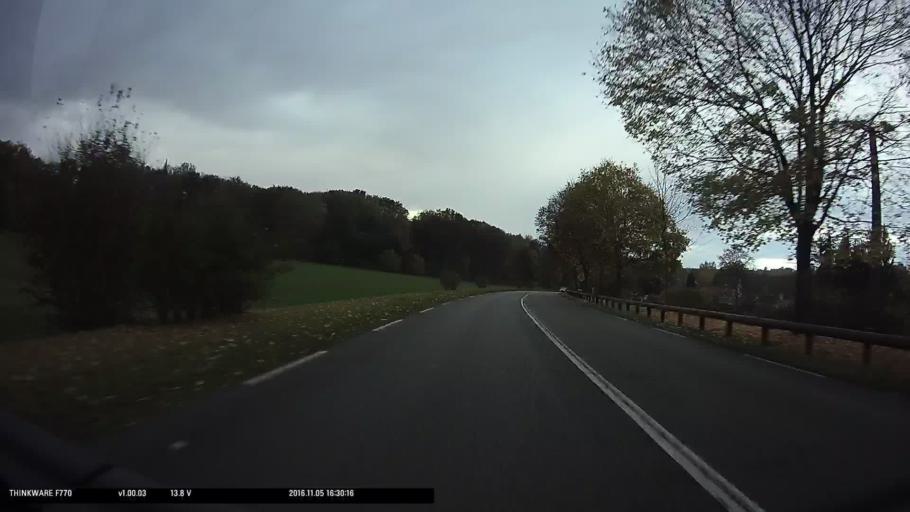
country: FR
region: Ile-de-France
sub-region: Departement du Val-d'Oise
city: Sagy
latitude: 49.0432
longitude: 1.9527
